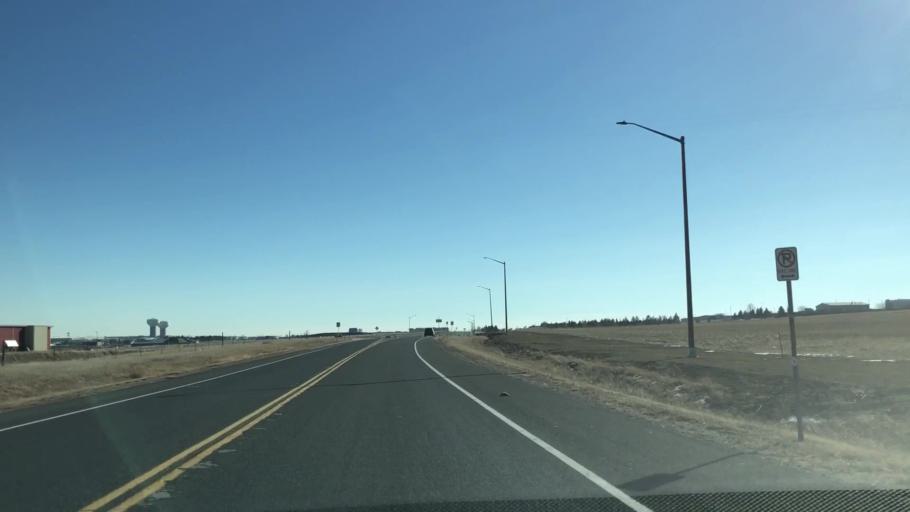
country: US
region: Colorado
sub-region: Weld County
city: Windsor
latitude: 40.4532
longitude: -104.9825
